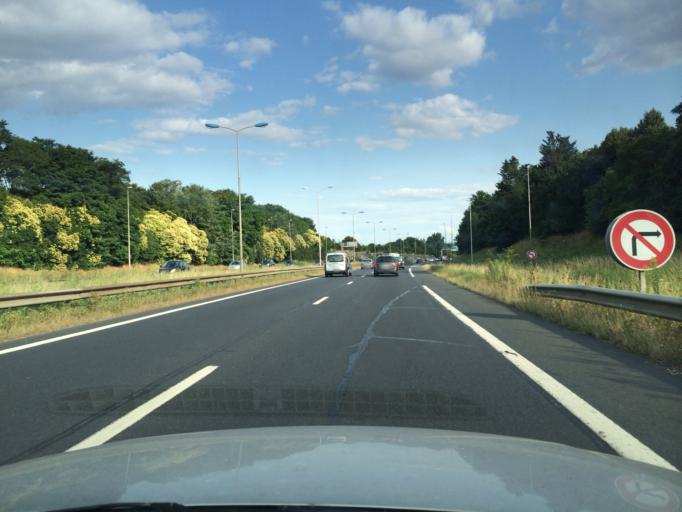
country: FR
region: Lower Normandy
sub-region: Departement du Calvados
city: Caen
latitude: 49.1986
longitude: -0.3431
